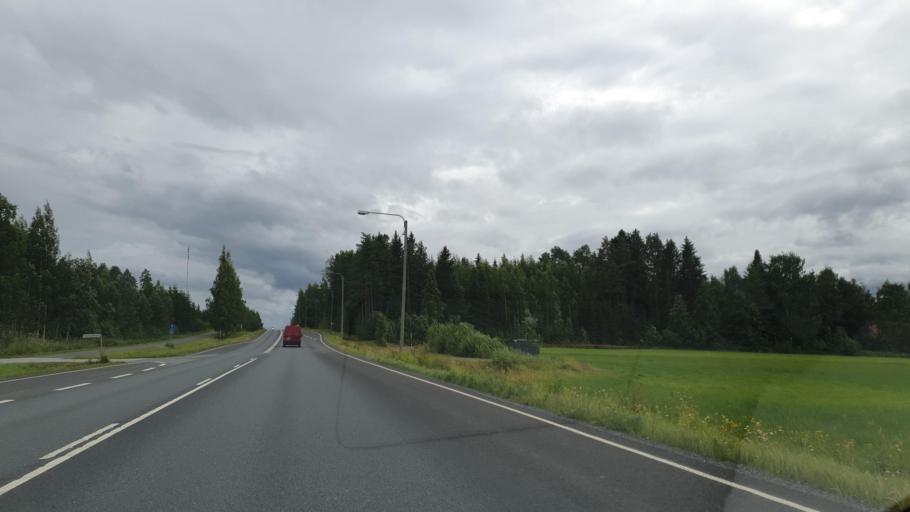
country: FI
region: Northern Savo
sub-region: Ylae-Savo
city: Lapinlahti
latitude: 63.4343
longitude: 27.3266
